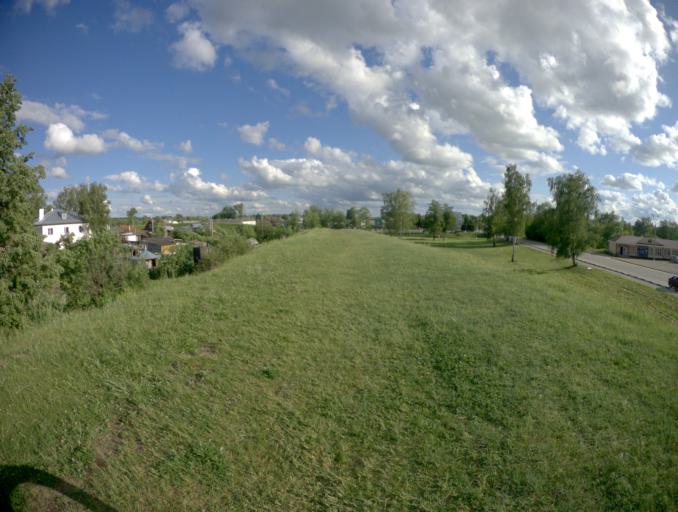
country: RU
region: Vladimir
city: Yur'yev-Pol'skiy
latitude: 56.4973
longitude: 39.6783
